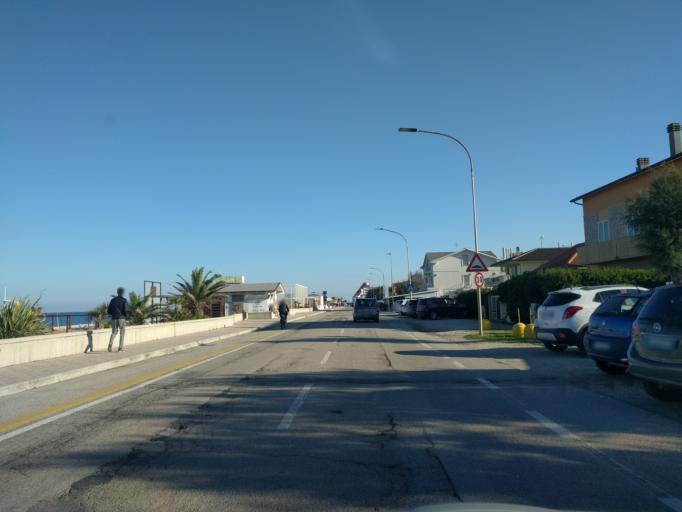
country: IT
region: The Marches
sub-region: Provincia di Pesaro e Urbino
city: Marotta
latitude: 43.7636
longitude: 13.1495
